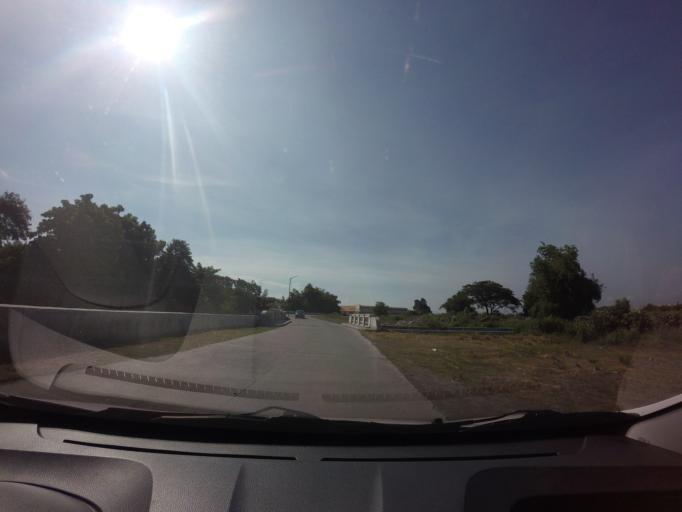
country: PH
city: Sambayanihan People's Village
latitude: 14.4727
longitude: 120.9860
